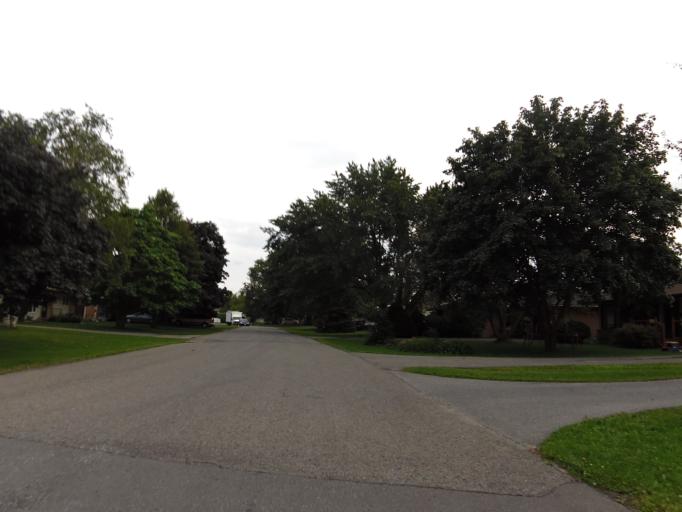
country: CA
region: Ontario
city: Bells Corners
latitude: 45.3173
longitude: -75.8214
